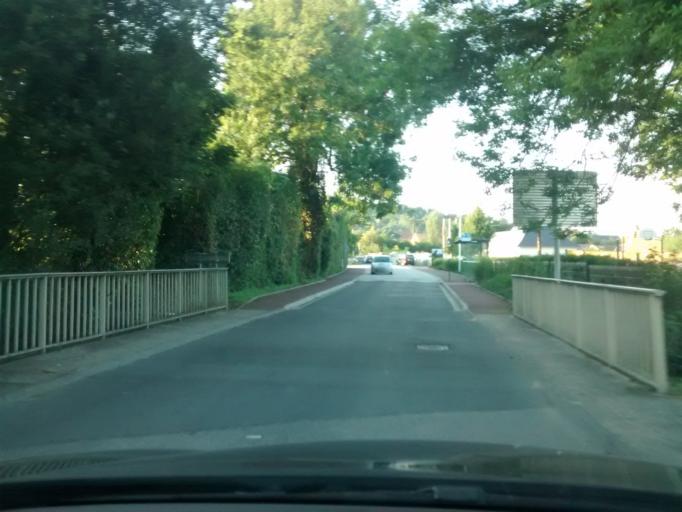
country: FR
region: Lower Normandy
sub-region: Departement du Calvados
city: Touques
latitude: 49.3280
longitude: 0.0859
